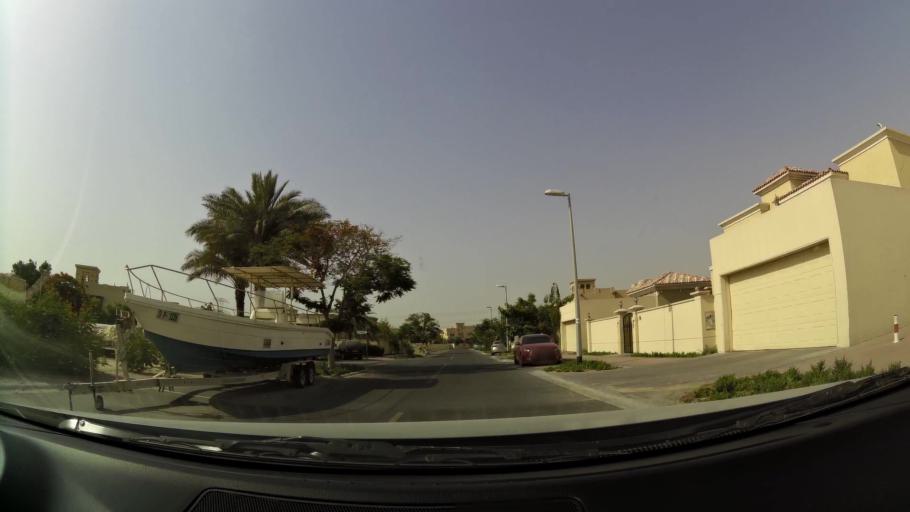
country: AE
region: Ash Shariqah
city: Sharjah
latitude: 25.2702
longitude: 55.4568
